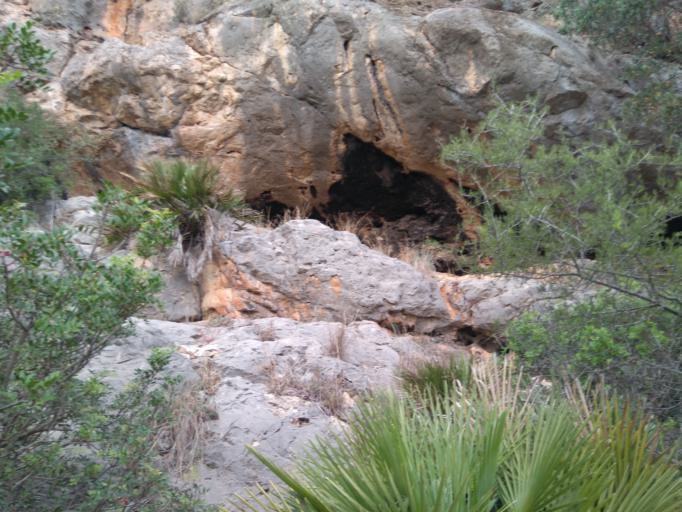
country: ES
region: Valencia
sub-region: Provincia de Valencia
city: Benimodo
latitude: 39.1993
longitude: -0.5884
